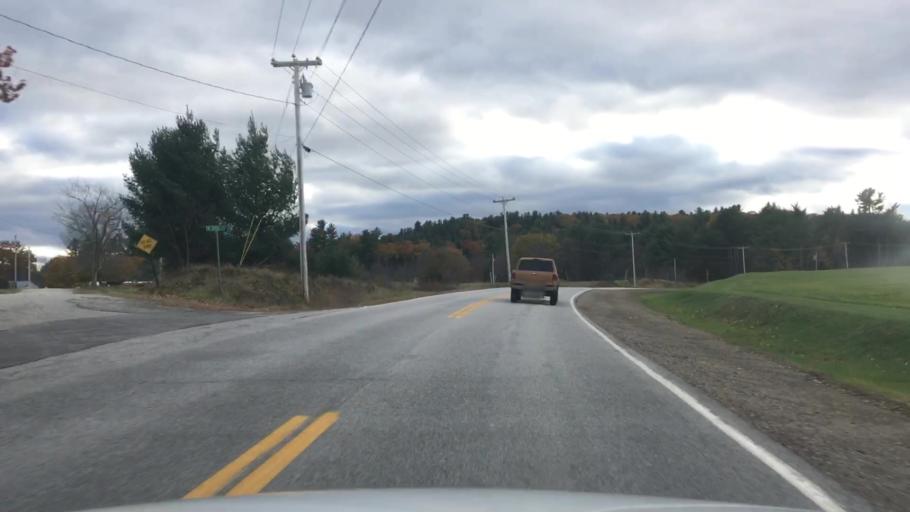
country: US
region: Maine
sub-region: Androscoggin County
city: Livermore
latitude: 44.3335
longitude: -70.2022
